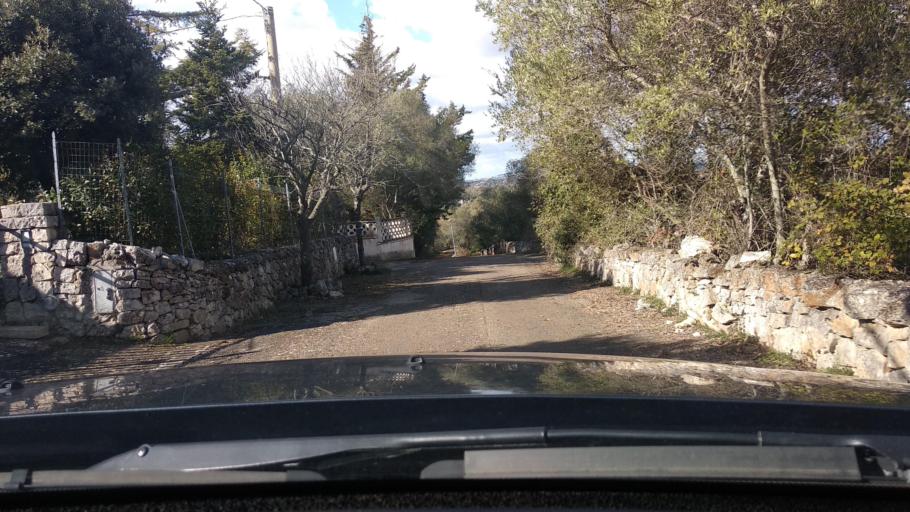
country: IT
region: Apulia
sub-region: Provincia di Brindisi
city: Casalini
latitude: 40.6909
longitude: 17.4861
